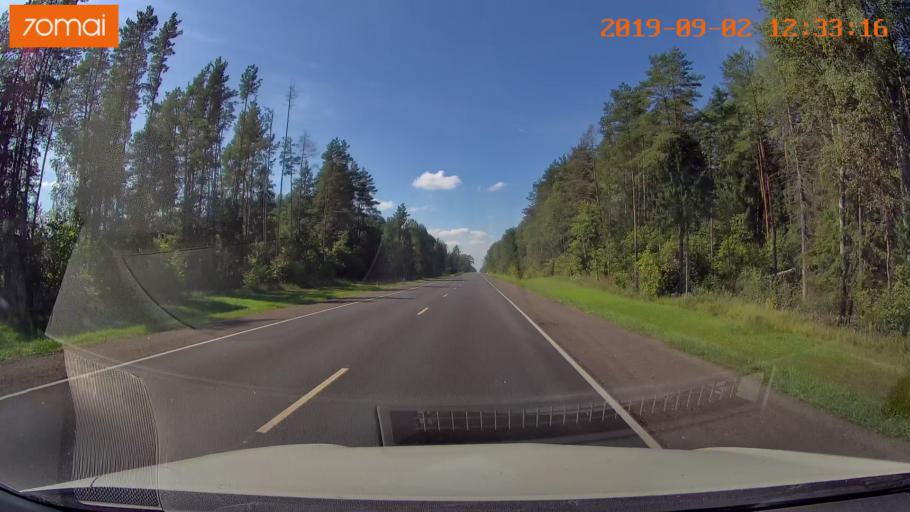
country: RU
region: Smolensk
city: Shumyachi
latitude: 53.8191
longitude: 32.4325
